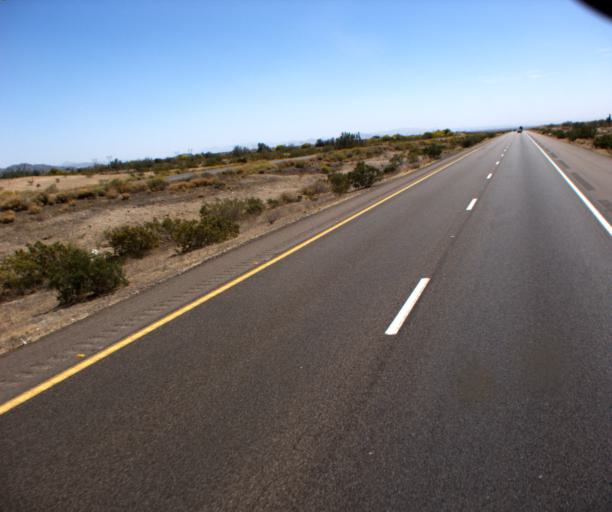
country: US
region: Arizona
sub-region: Maricopa County
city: Gila Bend
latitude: 33.0987
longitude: -112.6495
